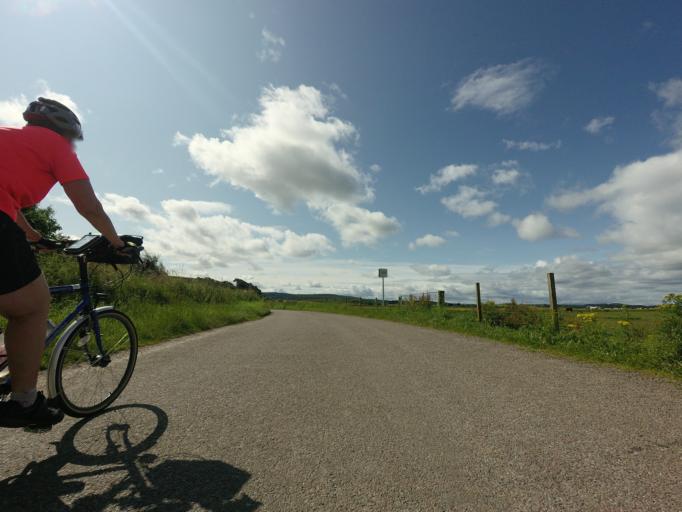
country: GB
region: Scotland
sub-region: Moray
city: Kinloss
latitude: 57.6437
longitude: -3.5220
